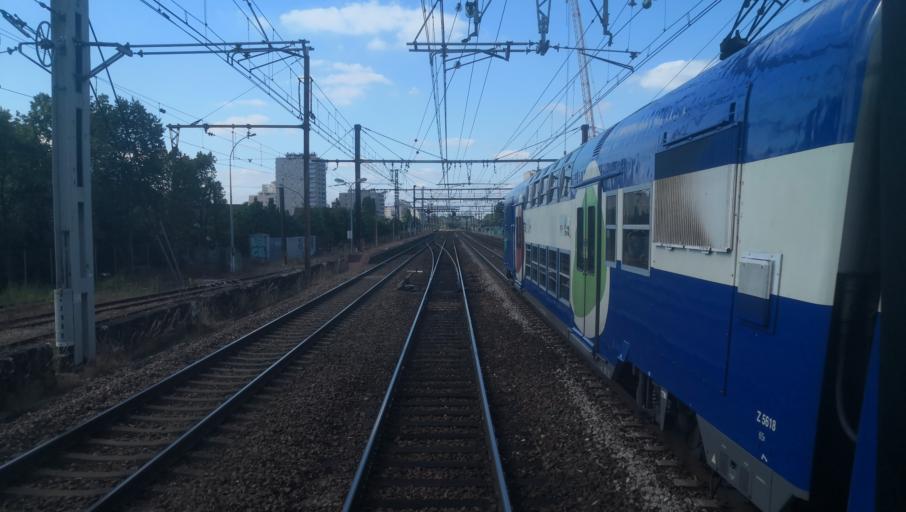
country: FR
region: Ile-de-France
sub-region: Departement du Val-de-Marne
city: Alfortville
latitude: 48.7875
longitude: 2.4324
